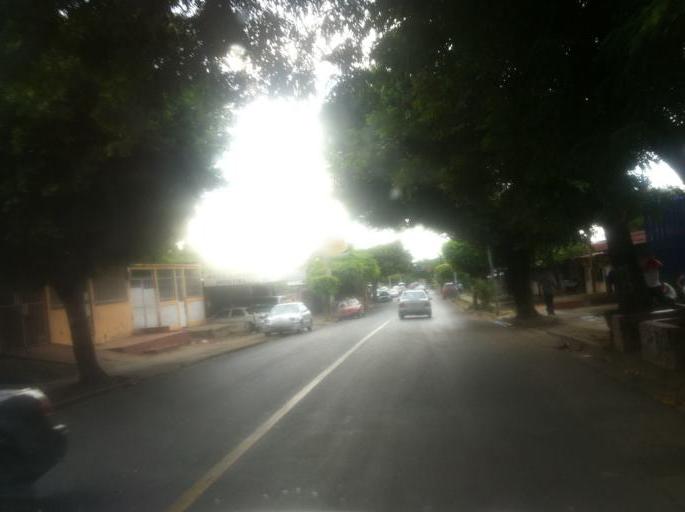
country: NI
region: Managua
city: Managua
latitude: 12.1188
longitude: -86.2398
